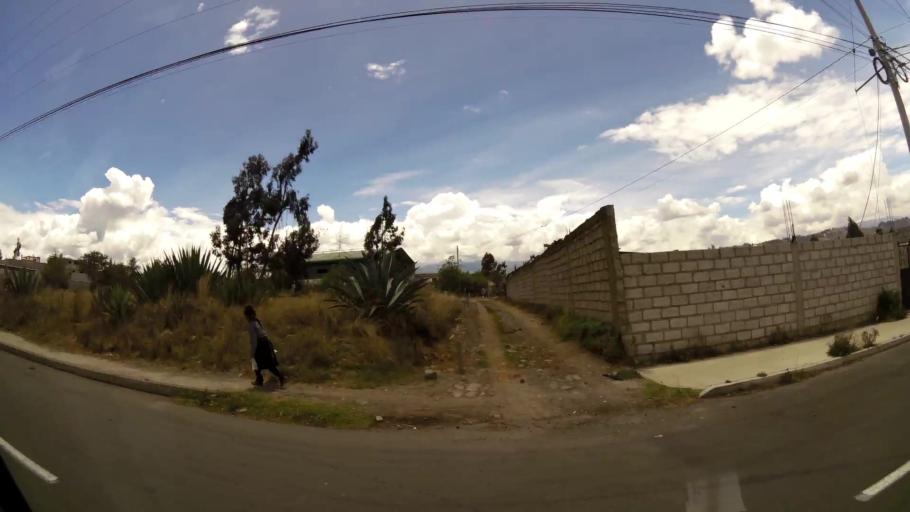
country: EC
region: Tungurahua
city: Ambato
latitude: -1.2702
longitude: -78.6059
